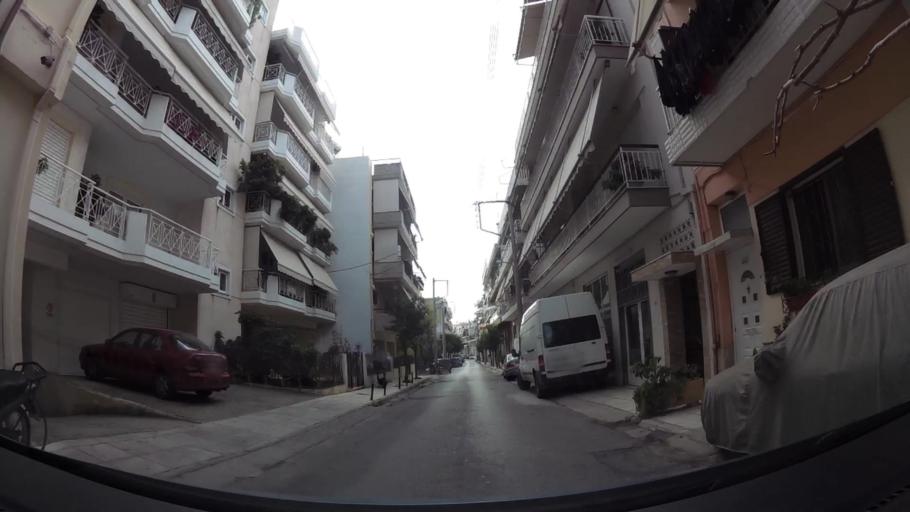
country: GR
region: Attica
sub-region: Nomarchia Athinas
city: Ilion
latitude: 38.0393
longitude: 23.7006
